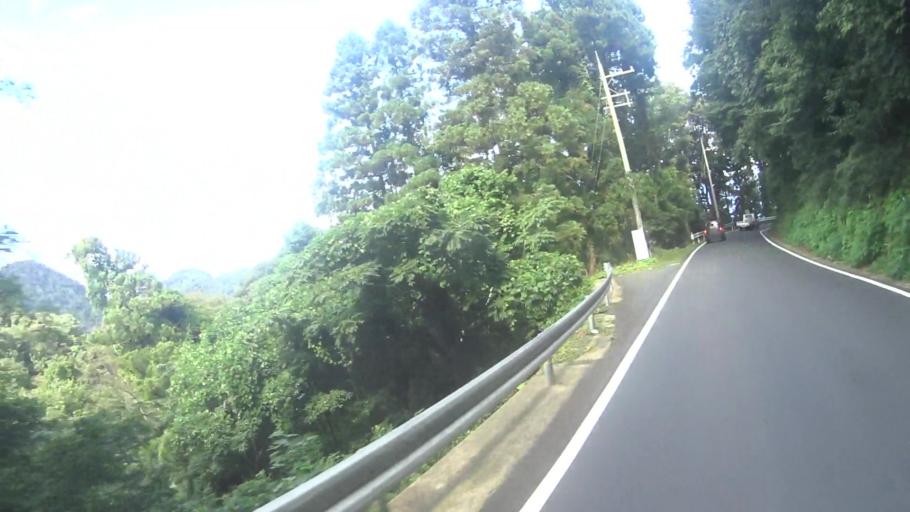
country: JP
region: Kyoto
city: Miyazu
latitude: 35.7479
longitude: 135.2501
